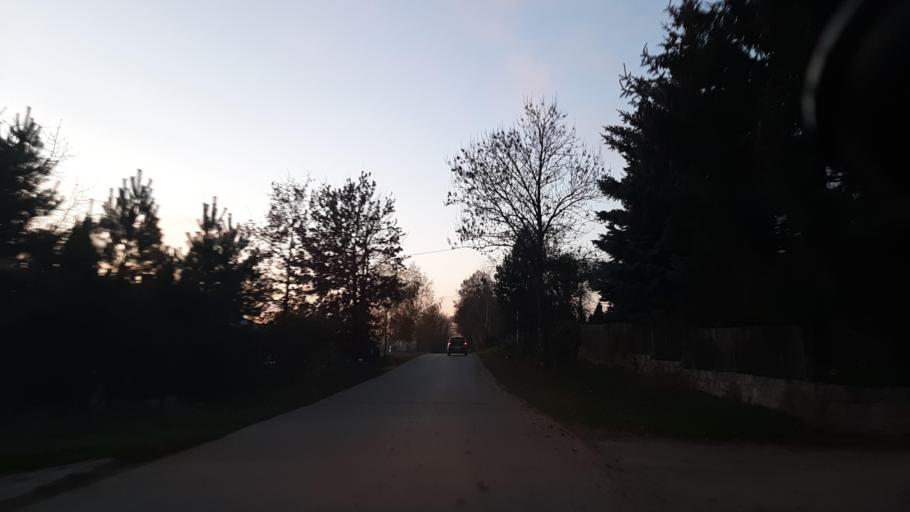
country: PL
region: Lublin Voivodeship
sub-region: Powiat lubelski
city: Jastkow
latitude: 51.3380
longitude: 22.4243
